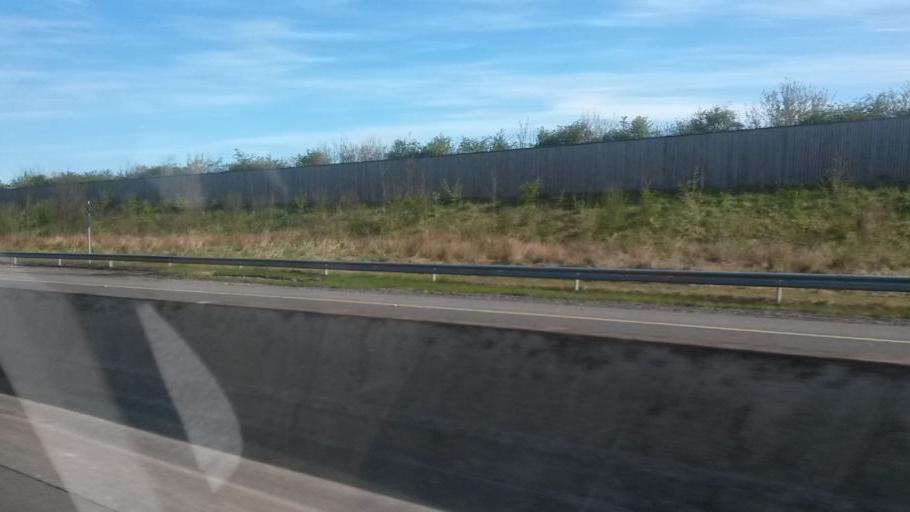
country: IE
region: Leinster
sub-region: An Mhi
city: Navan
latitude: 53.6032
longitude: -6.6408
